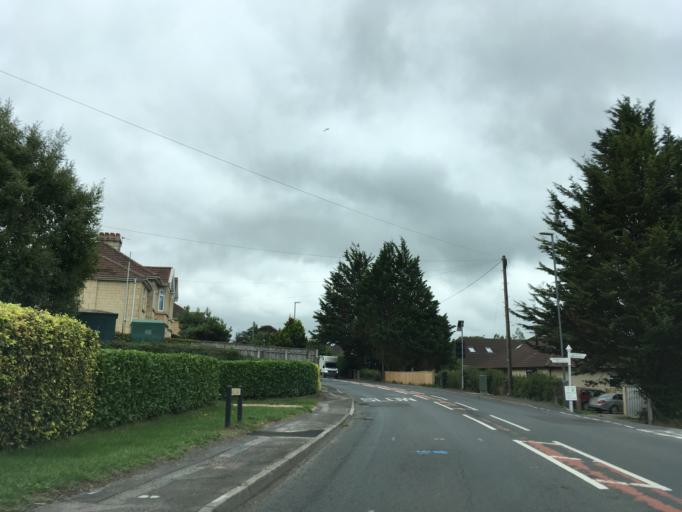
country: GB
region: England
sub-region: Bath and North East Somerset
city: Keynsham
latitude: 51.4046
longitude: -2.4930
